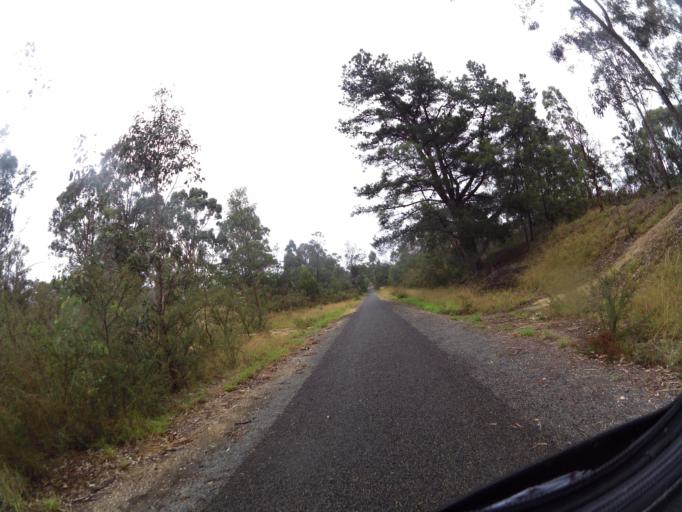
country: AU
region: Victoria
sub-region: East Gippsland
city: Bairnsdale
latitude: -37.8157
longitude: 147.7313
